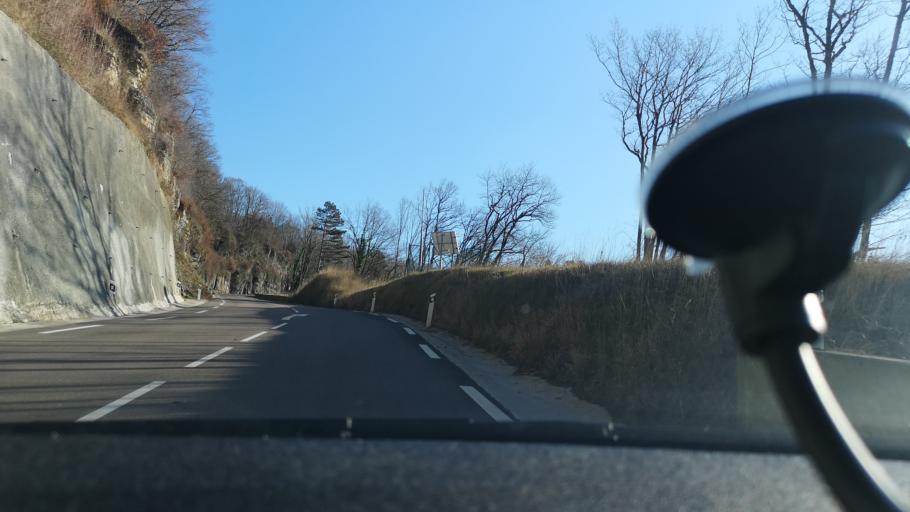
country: FR
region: Franche-Comte
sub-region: Departement du Jura
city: Poligny
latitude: 46.8210
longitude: 5.7361
